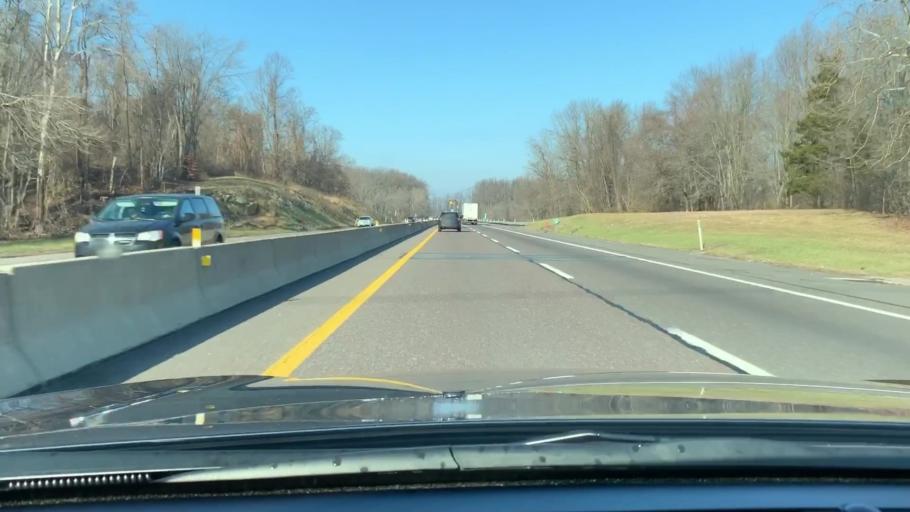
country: US
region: Pennsylvania
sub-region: Chester County
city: Elverson
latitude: 40.1084
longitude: -75.7580
